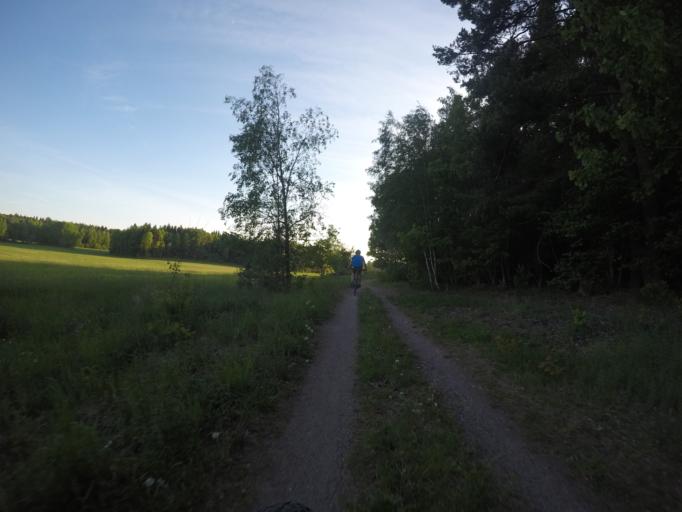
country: SE
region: Soedermanland
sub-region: Eskilstuna Kommun
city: Skogstorp
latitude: 59.3300
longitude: 16.4987
